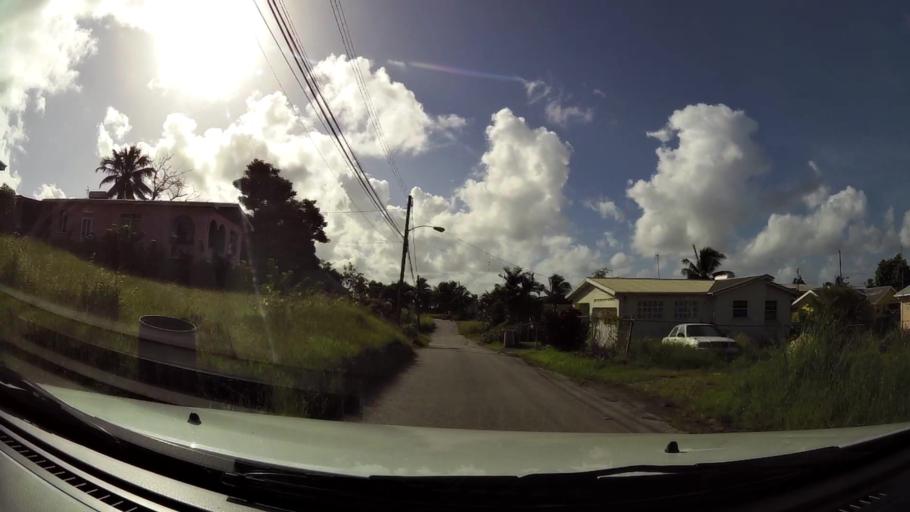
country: BB
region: Saint James
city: Holetown
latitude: 13.1545
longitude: -59.6077
